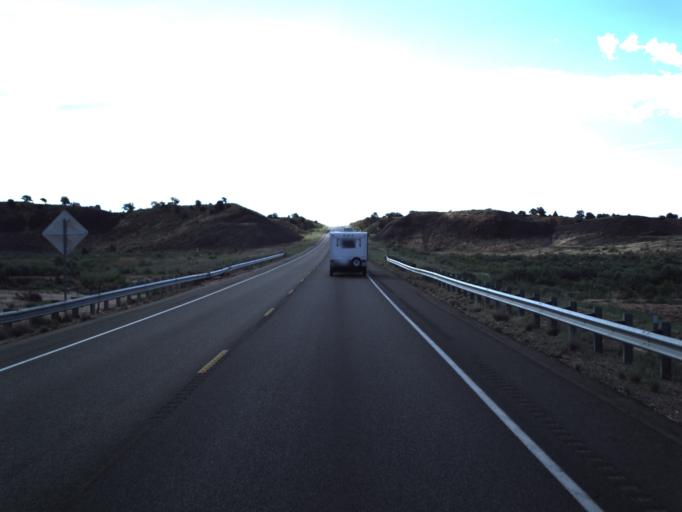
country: US
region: Utah
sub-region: Kane County
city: Kanab
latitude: 37.0377
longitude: -112.5046
